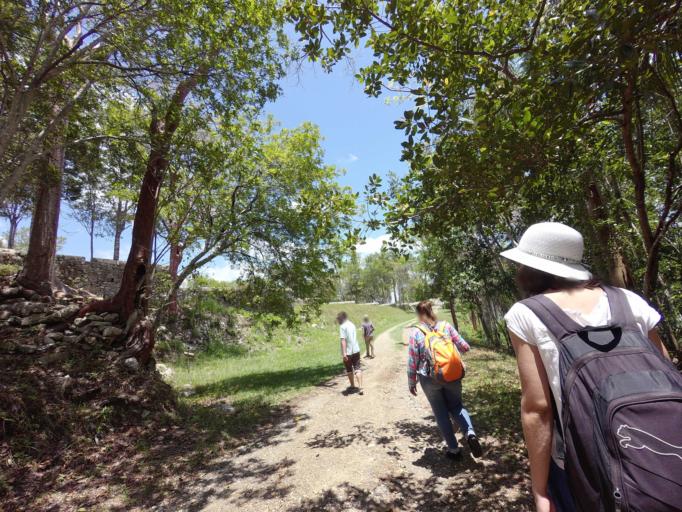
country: CU
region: Artemisa
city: Soroa
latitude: 22.8625
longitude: -82.9285
